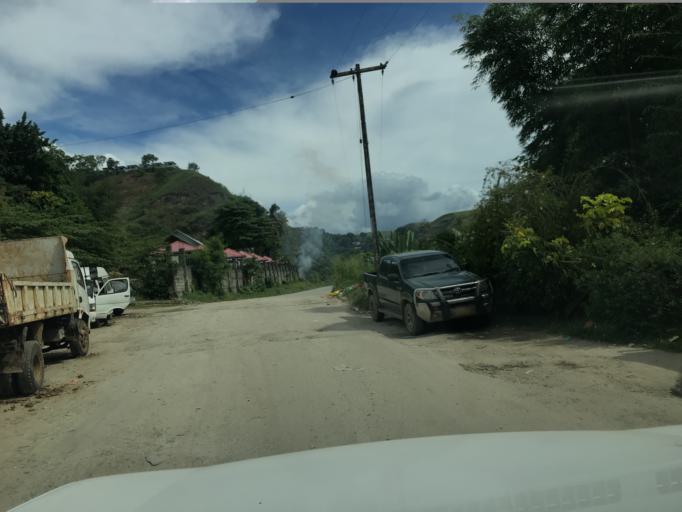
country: SB
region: Guadalcanal
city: Honiara
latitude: -9.4411
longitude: 159.9613
